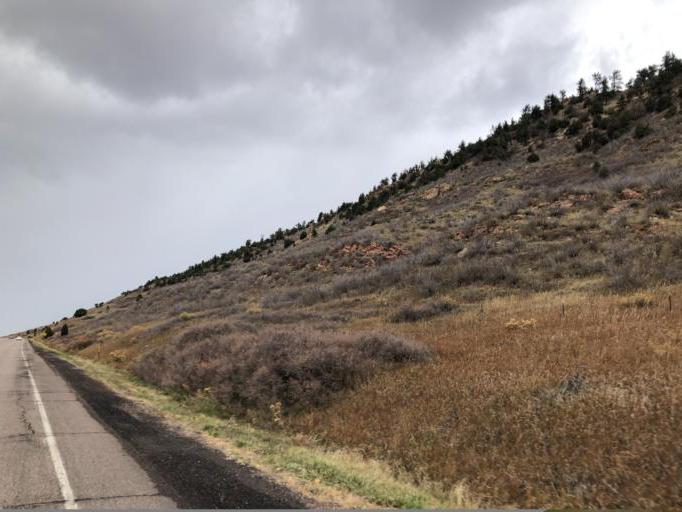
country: US
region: Colorado
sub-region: Jefferson County
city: West Pleasant View
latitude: 39.6842
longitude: -105.1991
